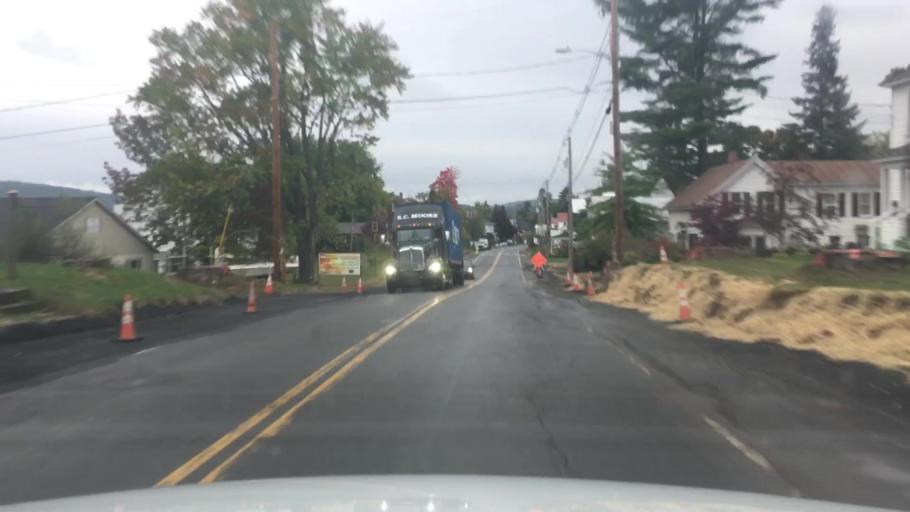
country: US
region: Maine
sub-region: Kennebec County
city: Rome
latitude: 44.5264
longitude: -69.8869
